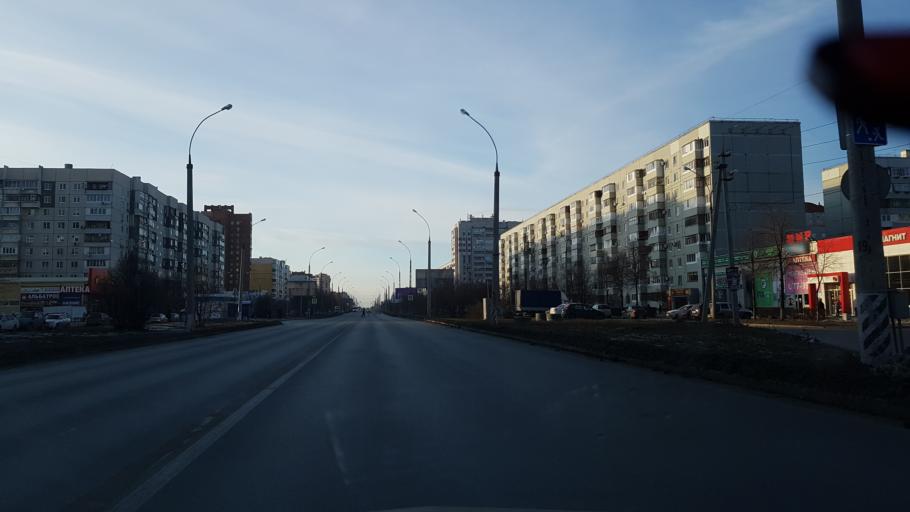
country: RU
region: Samara
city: Tol'yatti
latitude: 53.5401
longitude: 49.3572
